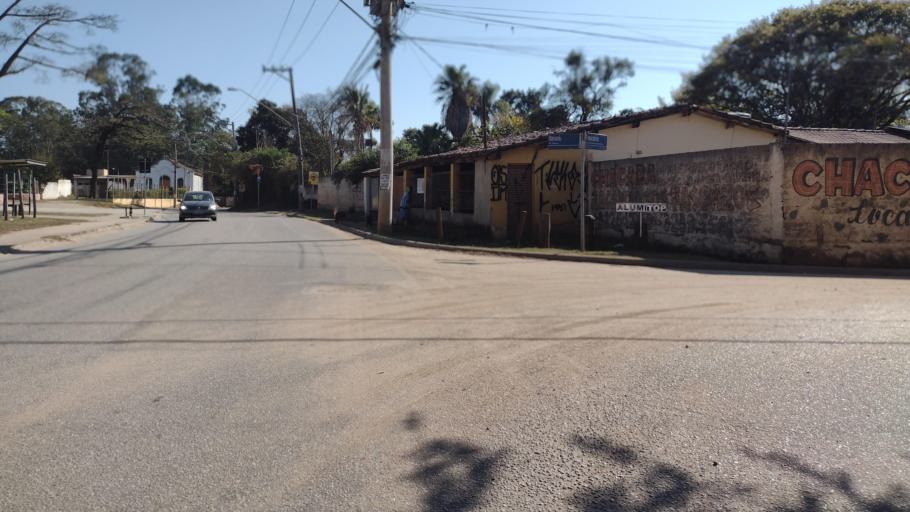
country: BR
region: Sao Paulo
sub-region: Sorocaba
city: Sorocaba
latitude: -23.4117
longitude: -47.4783
